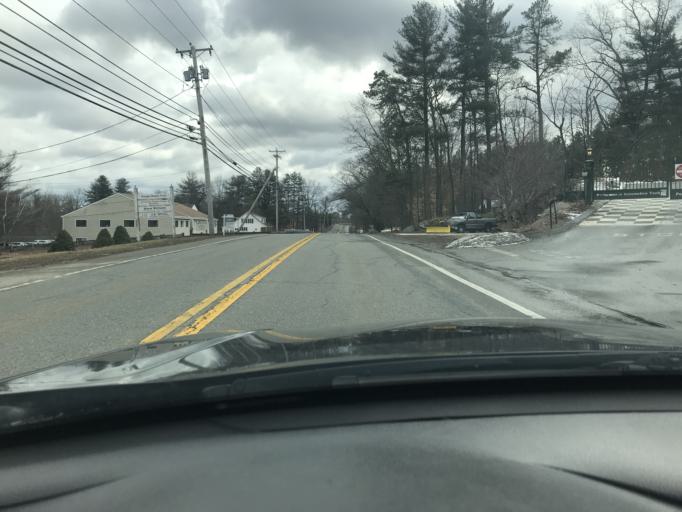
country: US
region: Massachusetts
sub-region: Middlesex County
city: Tyngsboro
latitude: 42.6591
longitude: -71.4050
